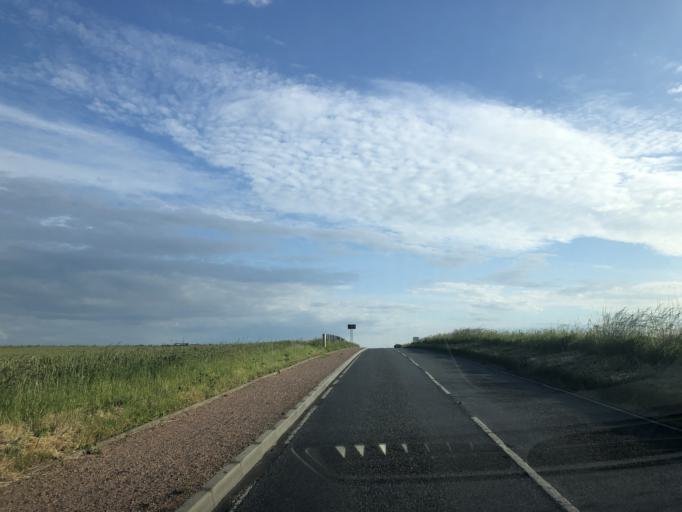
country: GB
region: Scotland
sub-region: Fife
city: Saint Monance
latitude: 56.2003
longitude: -2.7909
